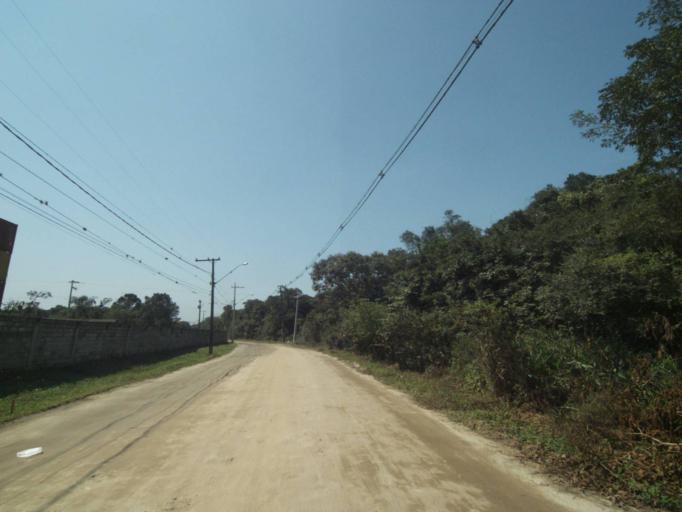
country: BR
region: Parana
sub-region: Paranagua
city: Paranagua
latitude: -25.5546
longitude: -48.5936
